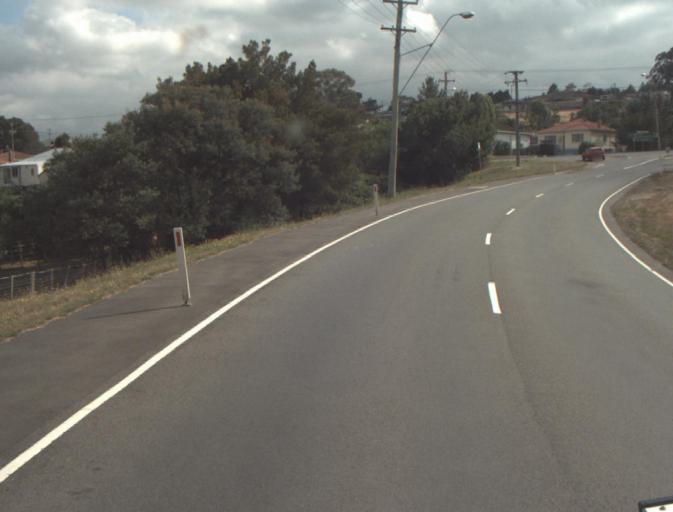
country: AU
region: Tasmania
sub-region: Launceston
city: Newstead
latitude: -41.4558
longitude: 147.1981
